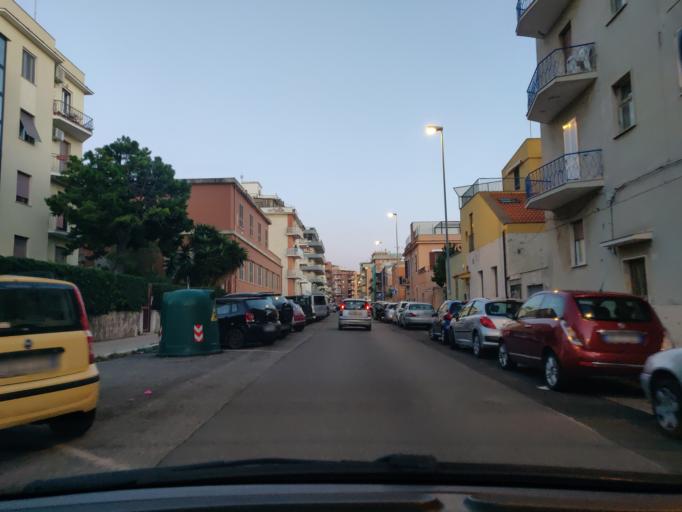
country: IT
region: Latium
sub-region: Citta metropolitana di Roma Capitale
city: Civitavecchia
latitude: 42.0897
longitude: 11.7995
